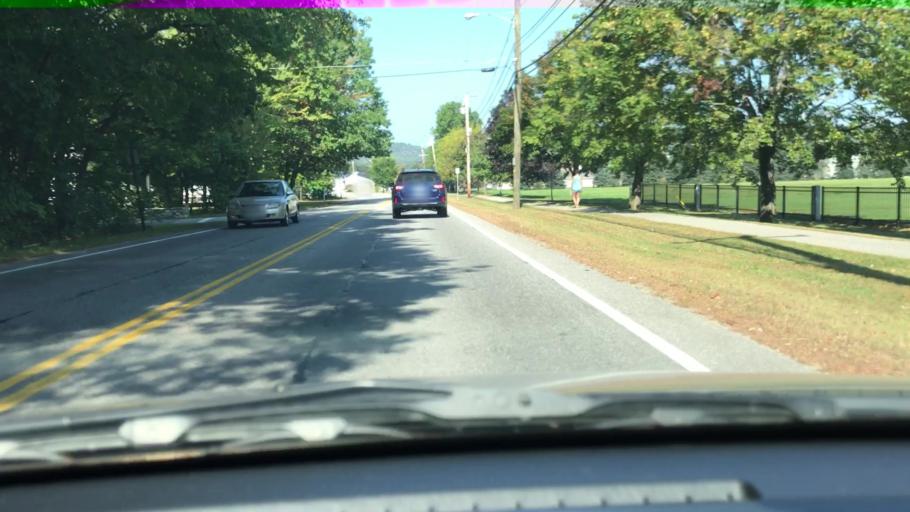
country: US
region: New Hampshire
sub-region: Cheshire County
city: Keene
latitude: 42.9464
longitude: -72.3168
